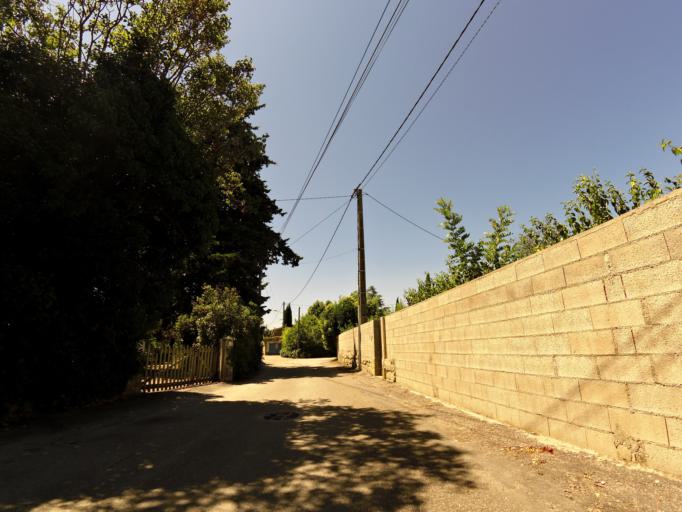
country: FR
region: Languedoc-Roussillon
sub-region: Departement du Gard
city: Aigues-Vives
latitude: 43.7388
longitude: 4.1711
